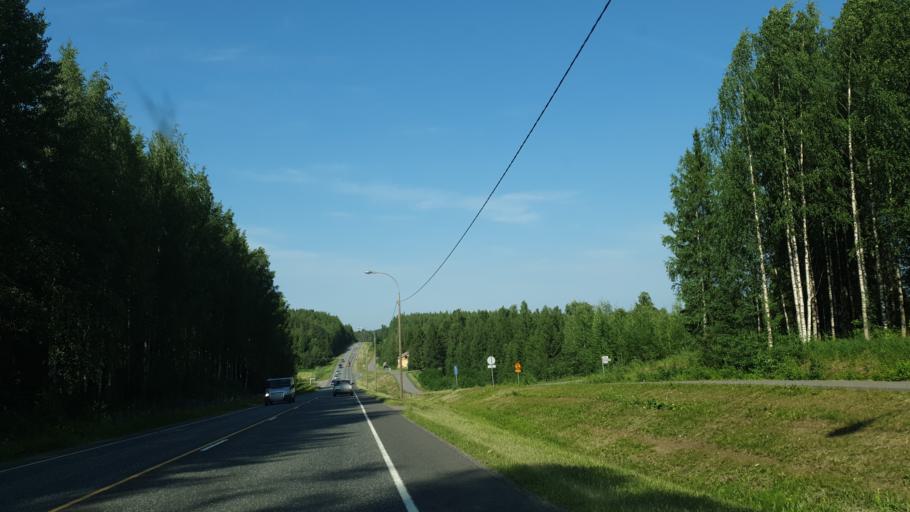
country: FI
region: Northern Savo
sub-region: Kuopio
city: Siilinjaervi
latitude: 63.1099
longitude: 27.7557
